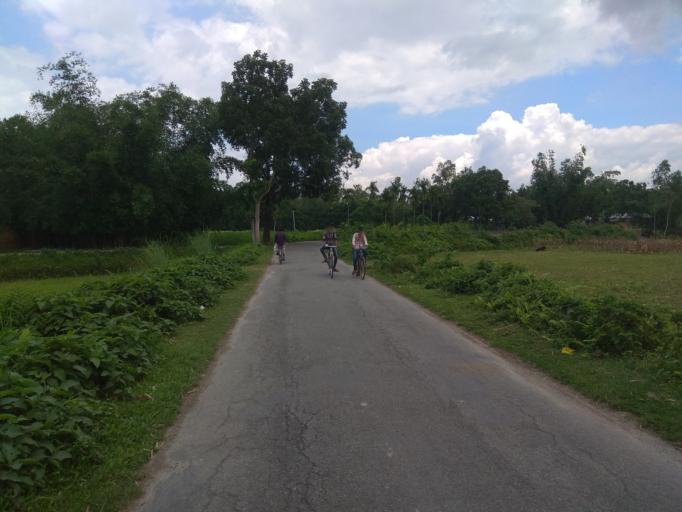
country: IN
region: West Bengal
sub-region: Koch Bihar
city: Haldibari
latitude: 26.2028
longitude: 88.9207
